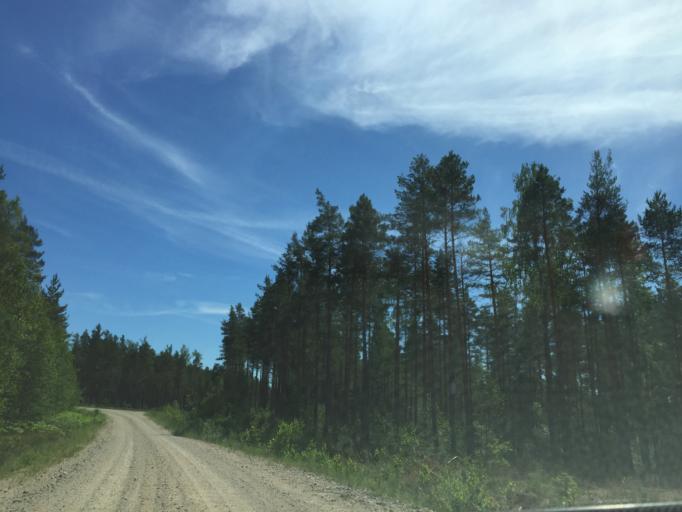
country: LV
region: Kuldigas Rajons
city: Kuldiga
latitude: 57.1093
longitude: 21.8789
